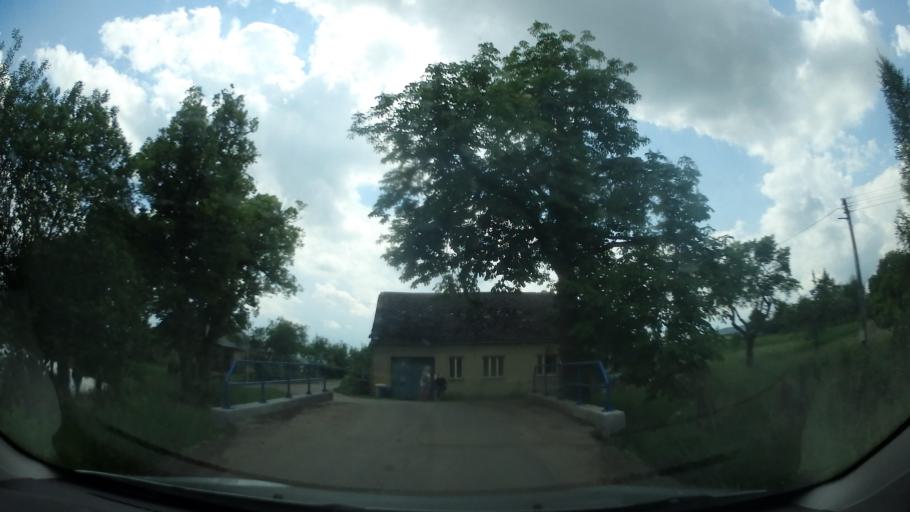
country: CZ
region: South Moravian
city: Velke Opatovice
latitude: 49.5640
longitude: 16.6734
